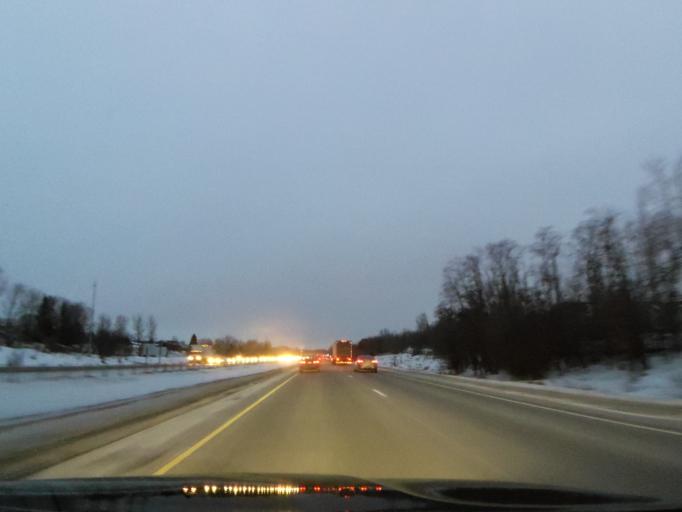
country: US
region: Minnesota
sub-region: Ramsey County
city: North Saint Paul
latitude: 45.0198
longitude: -92.9594
